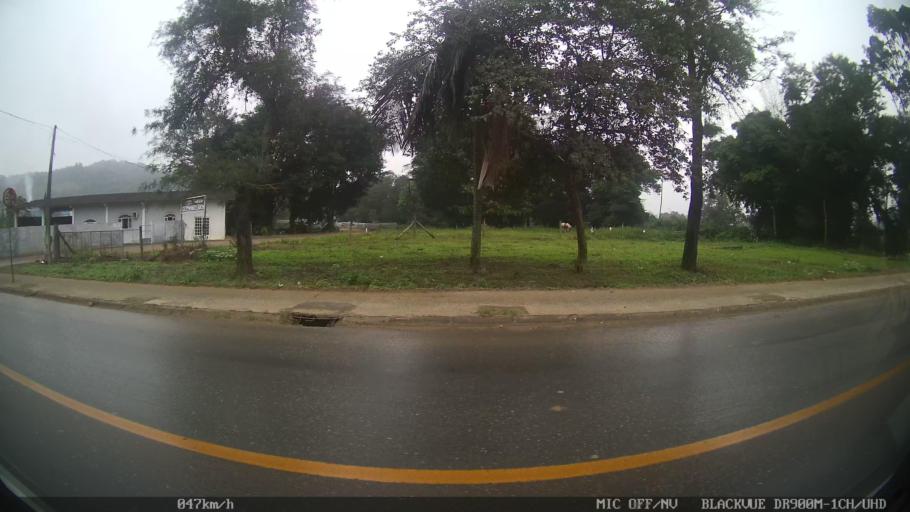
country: BR
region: Santa Catarina
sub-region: Joinville
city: Joinville
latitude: -26.2243
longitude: -48.8205
